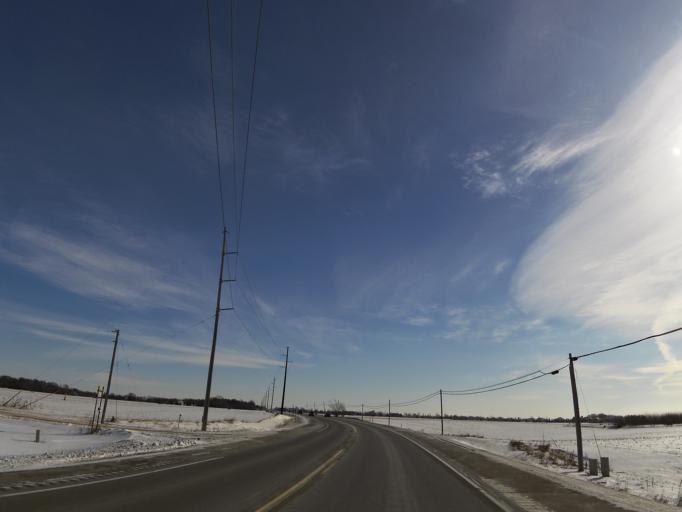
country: US
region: Minnesota
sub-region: Washington County
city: Cottage Grove
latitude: 44.7424
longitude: -92.9853
